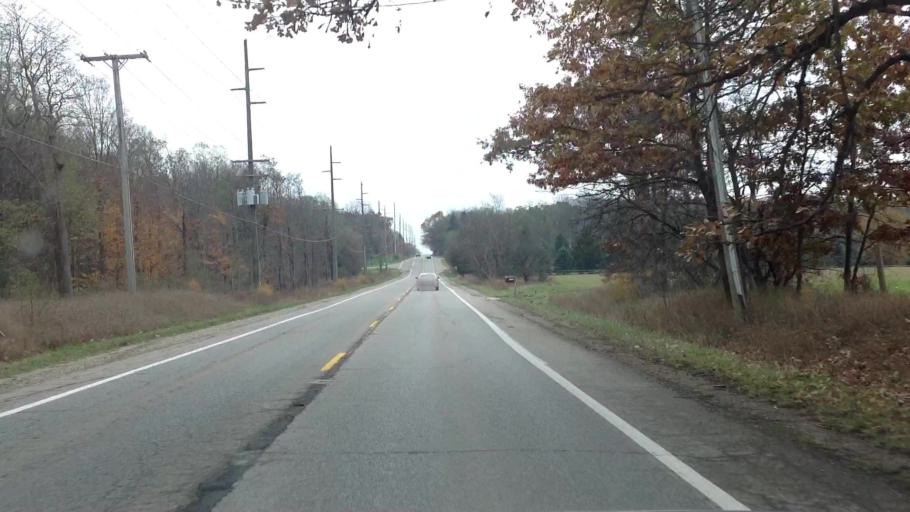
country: US
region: Michigan
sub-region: Oakland County
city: Milford
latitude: 42.6203
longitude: -83.6611
